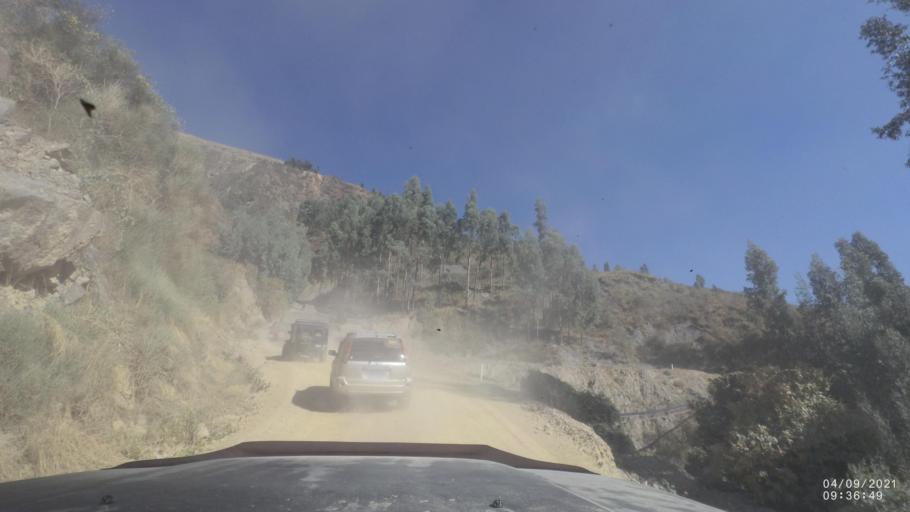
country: BO
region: Cochabamba
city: Sipe Sipe
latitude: -17.3493
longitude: -66.3828
